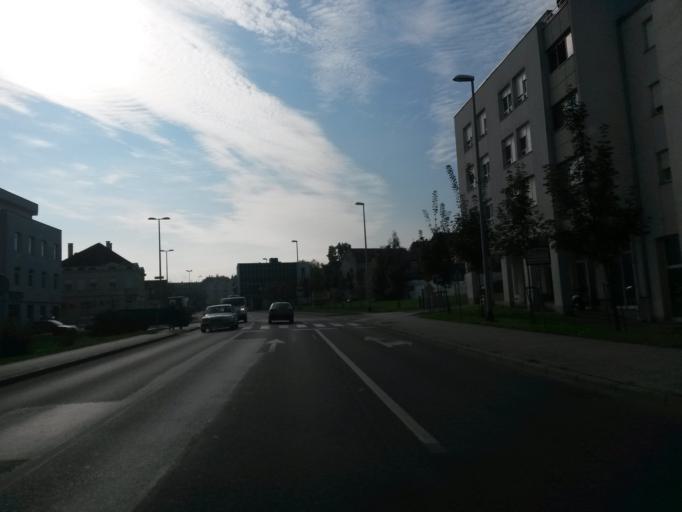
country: HR
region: Vukovarsko-Srijemska
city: Vukovar
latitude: 45.3502
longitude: 19.0020
